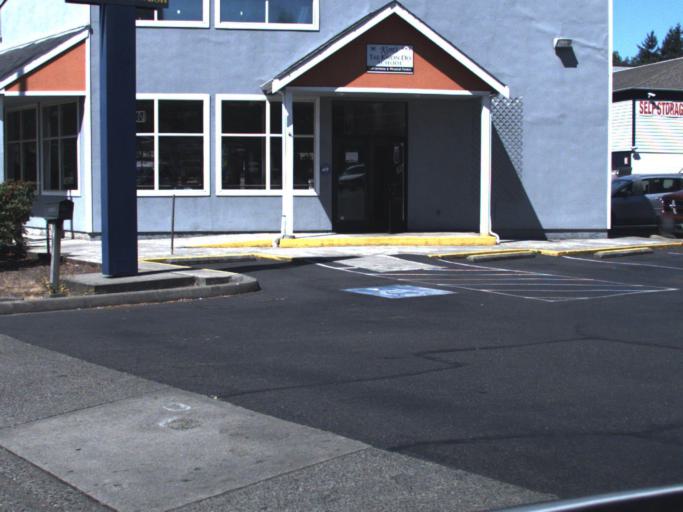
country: US
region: Washington
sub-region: King County
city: Newcastle
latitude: 47.5054
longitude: -122.1575
